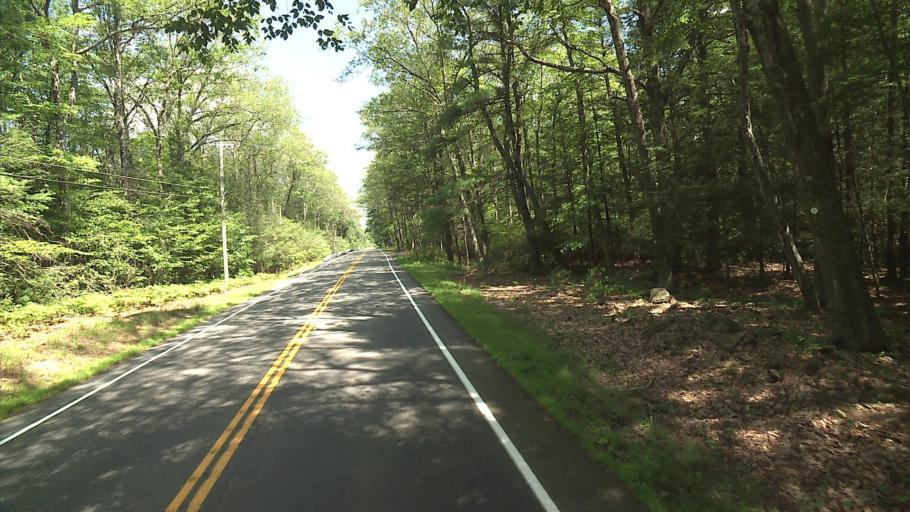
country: US
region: Massachusetts
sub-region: Worcester County
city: Southbridge
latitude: 42.0038
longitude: -72.0828
